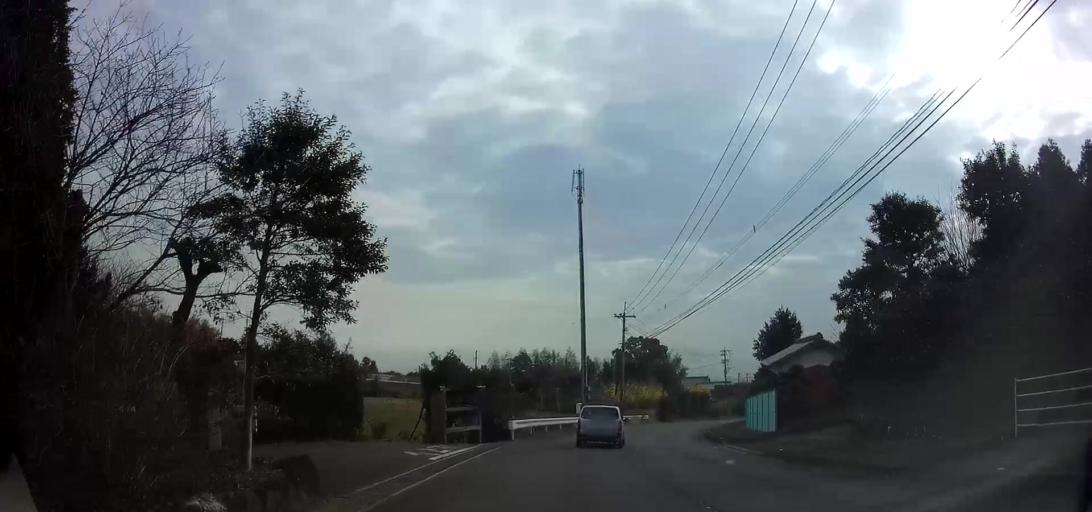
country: JP
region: Nagasaki
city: Shimabara
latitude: 32.6889
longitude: 130.2631
